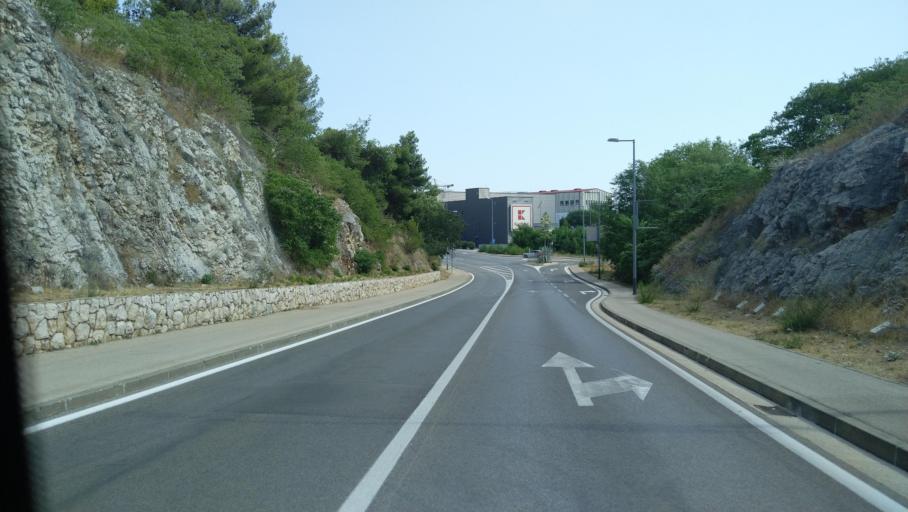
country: HR
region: Sibensko-Kniniska
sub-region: Grad Sibenik
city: Sibenik
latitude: 43.7248
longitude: 15.9044
